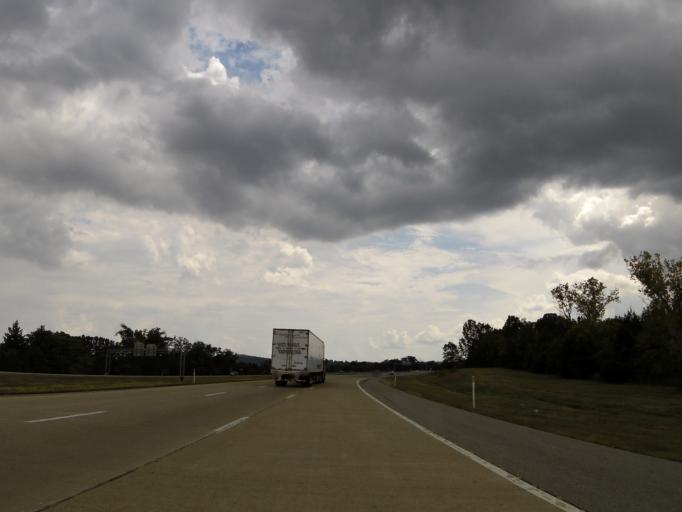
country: US
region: Tennessee
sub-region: Wilson County
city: Lebanon
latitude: 36.1801
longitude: -86.3528
